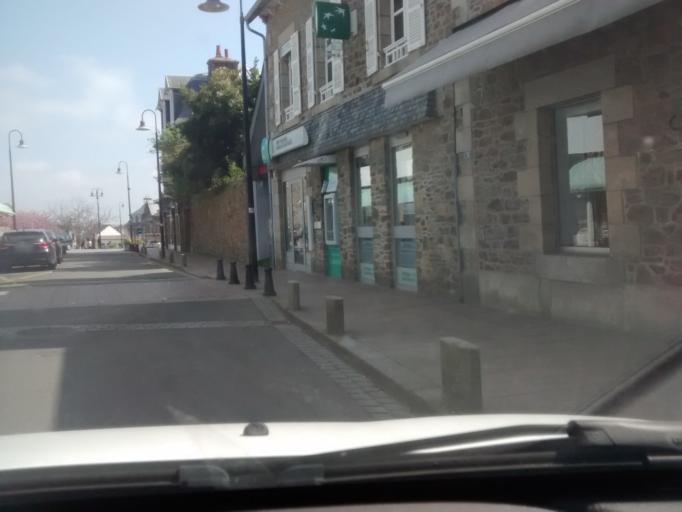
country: FR
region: Brittany
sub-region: Departement des Cotes-d'Armor
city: Perros-Guirec
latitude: 48.8145
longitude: -3.4451
